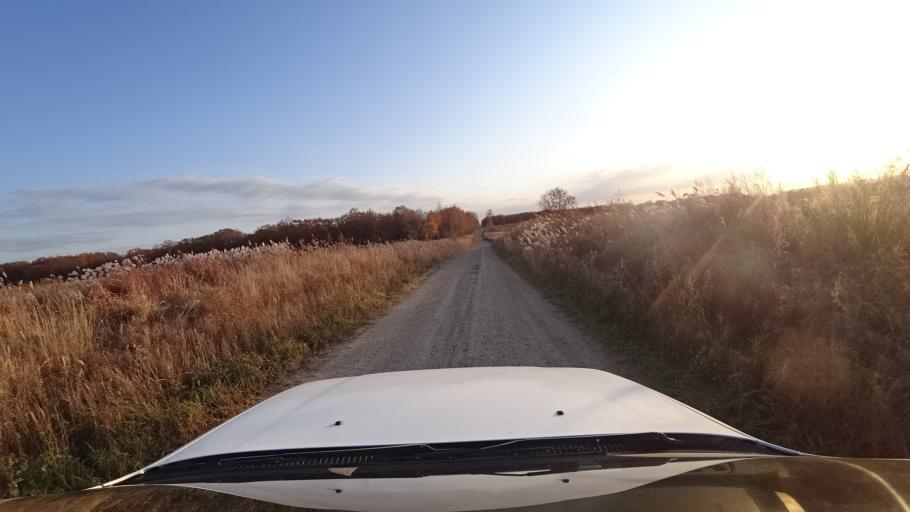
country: RU
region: Primorskiy
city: Lazo
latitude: 45.8084
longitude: 133.6067
